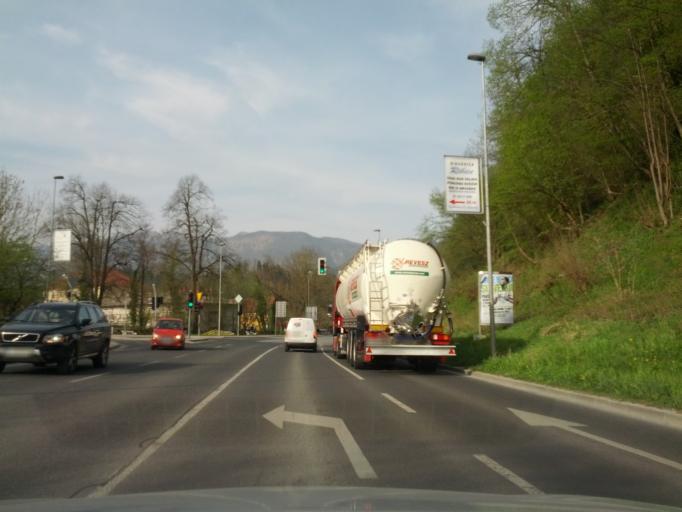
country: SI
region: Kamnik
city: Kamnik
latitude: 46.2251
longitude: 14.6144
